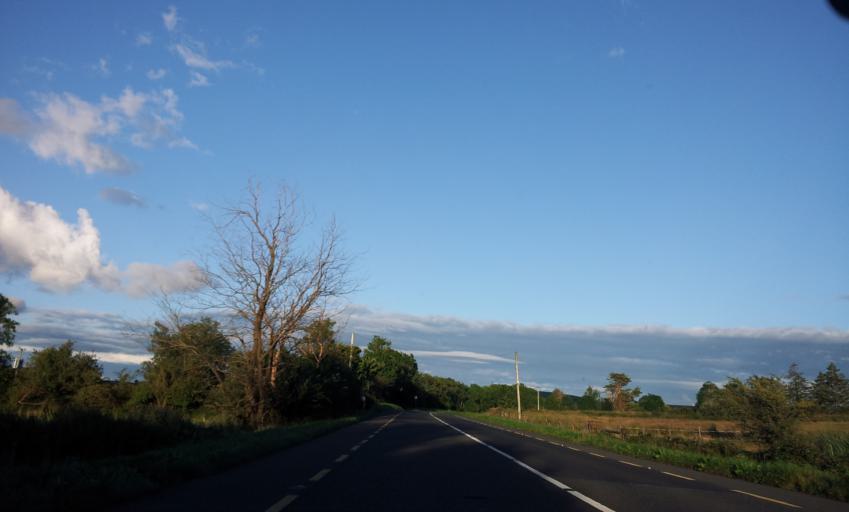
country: IE
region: Munster
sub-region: County Limerick
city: Abbeyfeale
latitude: 52.3876
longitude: -9.2440
